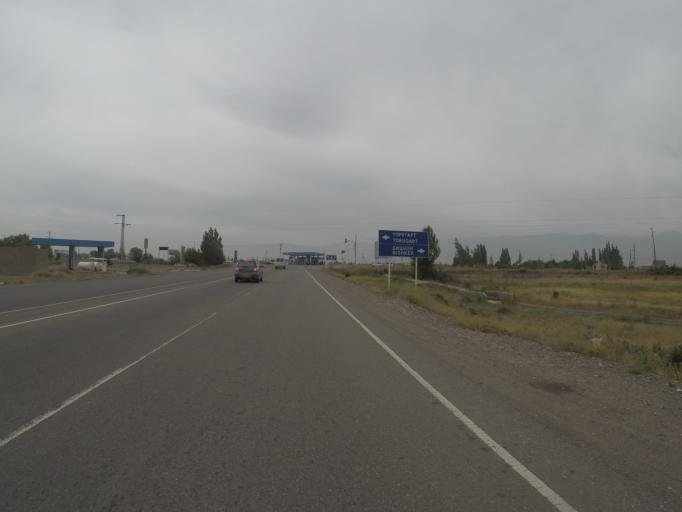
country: KG
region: Chuy
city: Bystrovka
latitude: 42.8247
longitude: 75.5446
